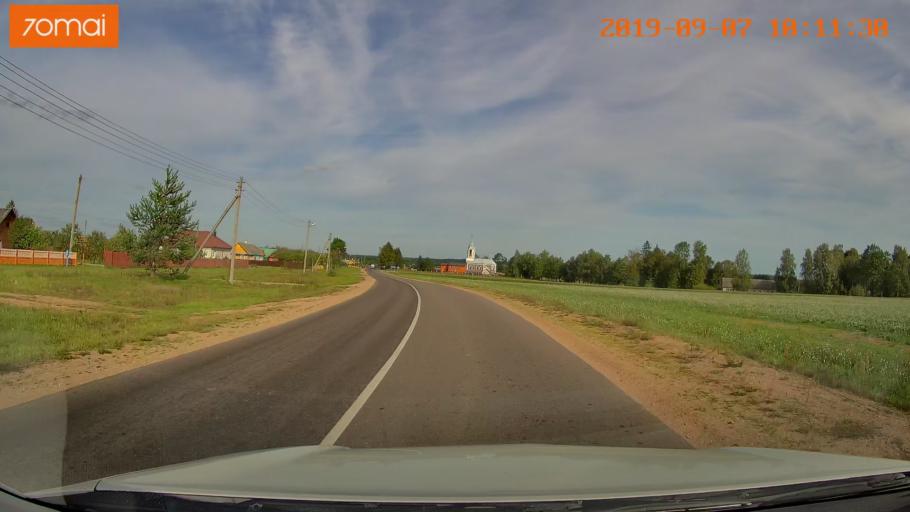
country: BY
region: Grodnenskaya
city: Voranava
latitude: 54.1238
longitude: 25.3657
